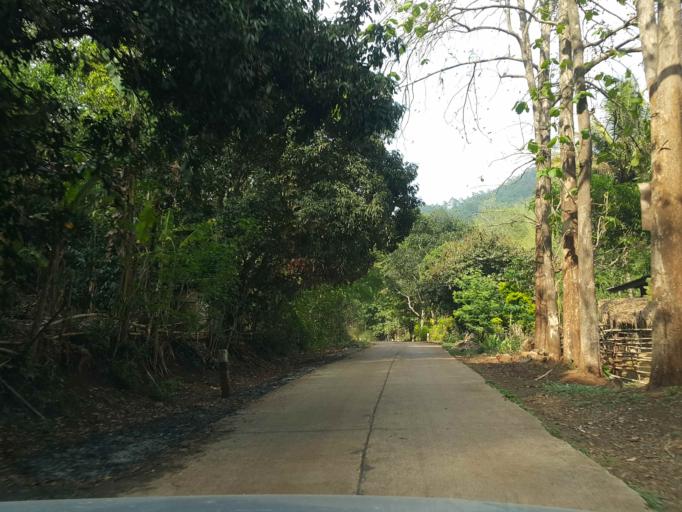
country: TH
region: Chiang Mai
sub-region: Amphoe Chiang Dao
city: Chiang Dao
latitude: 19.4039
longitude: 98.7836
